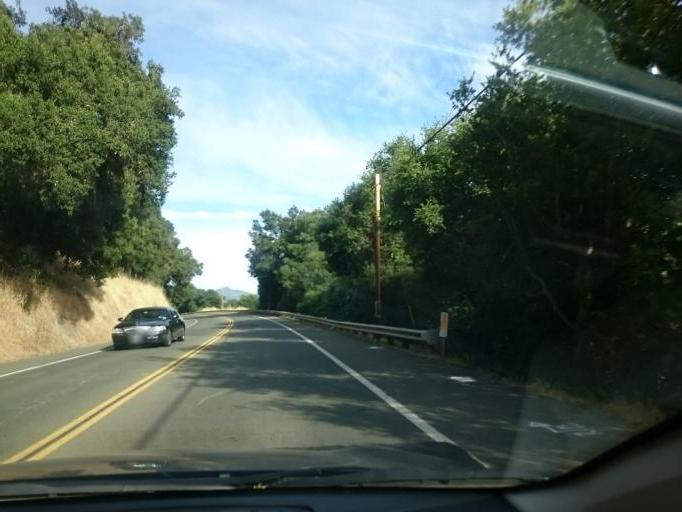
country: US
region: California
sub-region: Napa County
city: Saint Helena
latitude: 38.4995
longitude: -122.4294
